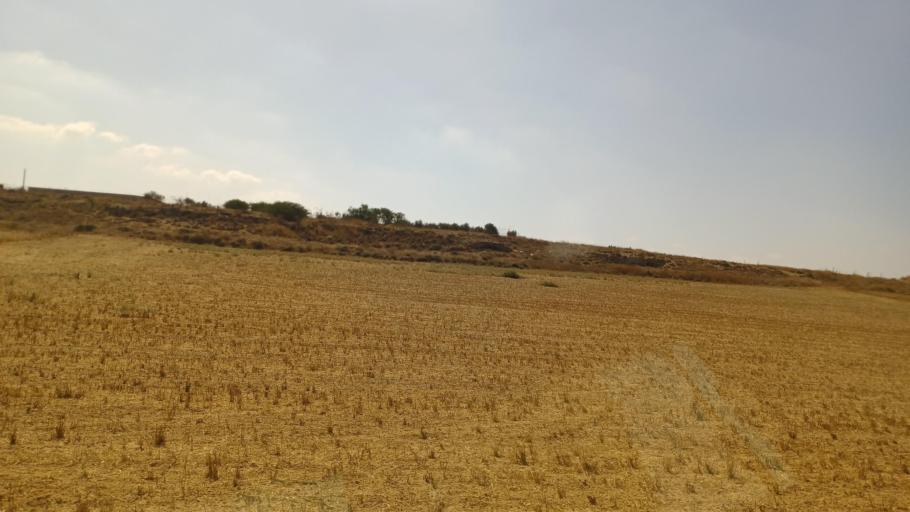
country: CY
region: Ammochostos
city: Acheritou
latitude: 35.0706
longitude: 33.8646
